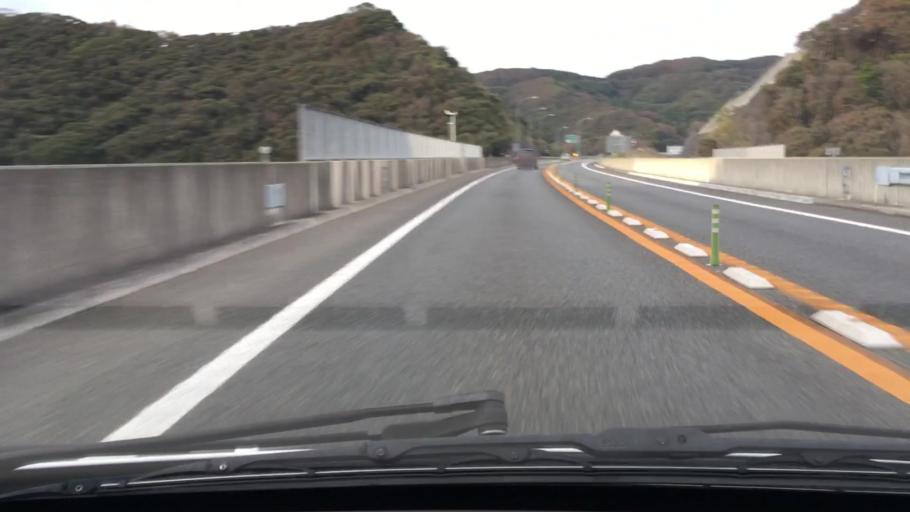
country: JP
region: Chiba
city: Futtsu
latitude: 35.1659
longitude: 139.8311
